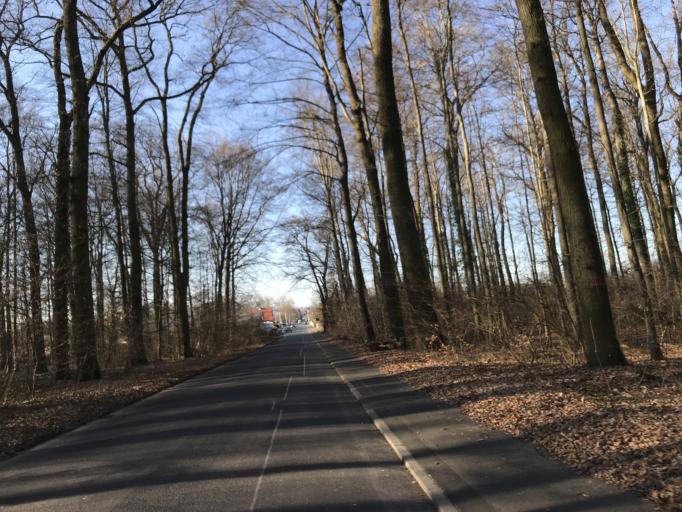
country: DE
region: Hesse
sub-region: Regierungsbezirk Darmstadt
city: Nidda
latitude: 50.4276
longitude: 8.9941
